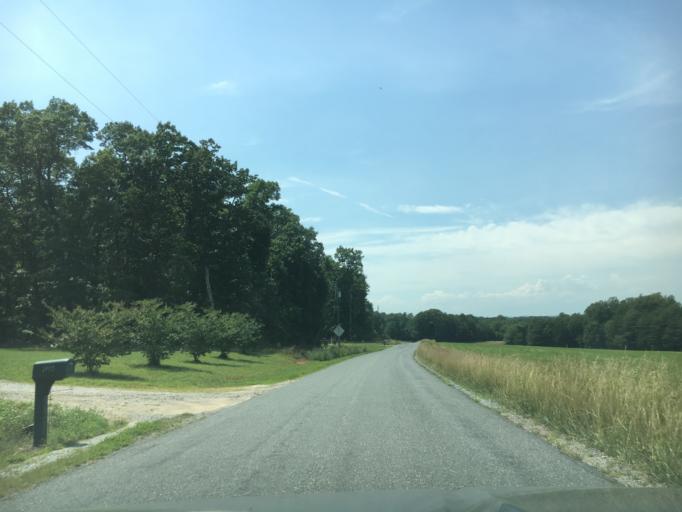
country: US
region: Virginia
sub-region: Pittsylvania County
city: Gretna
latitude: 36.9078
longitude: -79.4113
